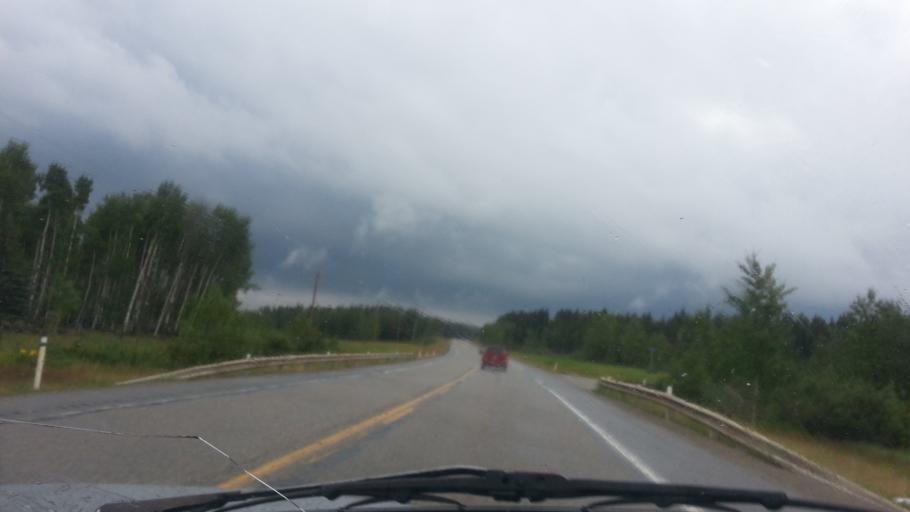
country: CA
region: Alberta
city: Cochrane
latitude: 50.9214
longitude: -114.5797
